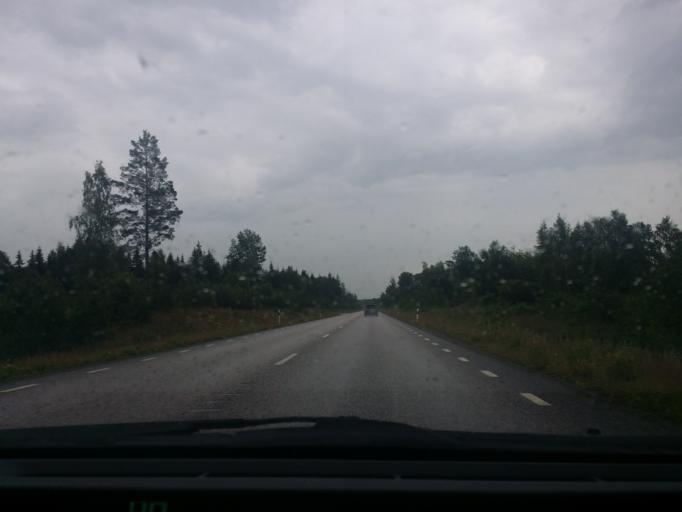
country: SE
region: OErebro
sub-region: Lindesbergs Kommun
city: Frovi
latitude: 59.4757
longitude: 15.3893
